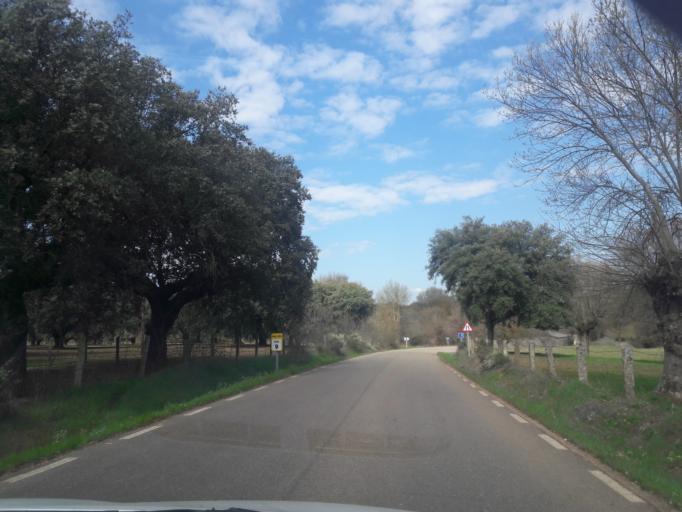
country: ES
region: Castille and Leon
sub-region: Provincia de Salamanca
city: Zamarra
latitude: 40.5563
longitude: -6.4510
